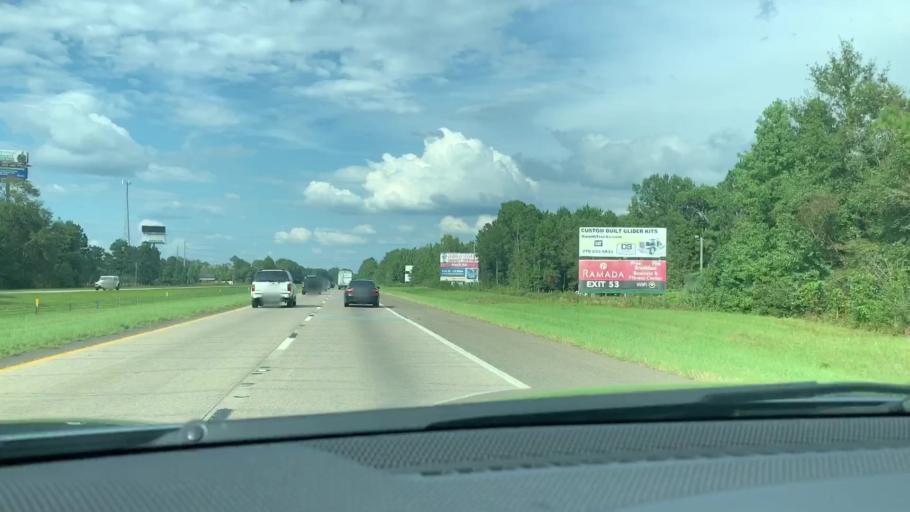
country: US
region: South Carolina
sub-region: Hampton County
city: Yemassee
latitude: 32.6797
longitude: -80.8819
